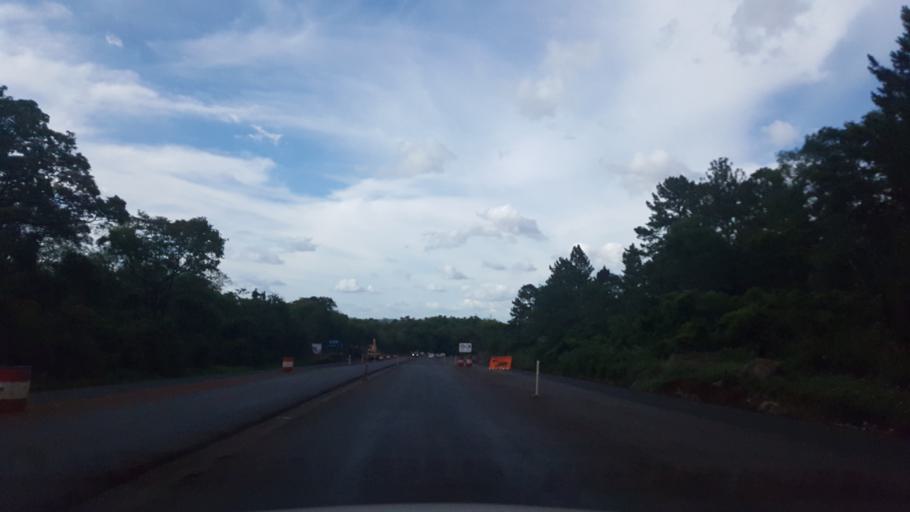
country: AR
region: Misiones
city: Santa Ana
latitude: -27.4014
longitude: -55.6024
